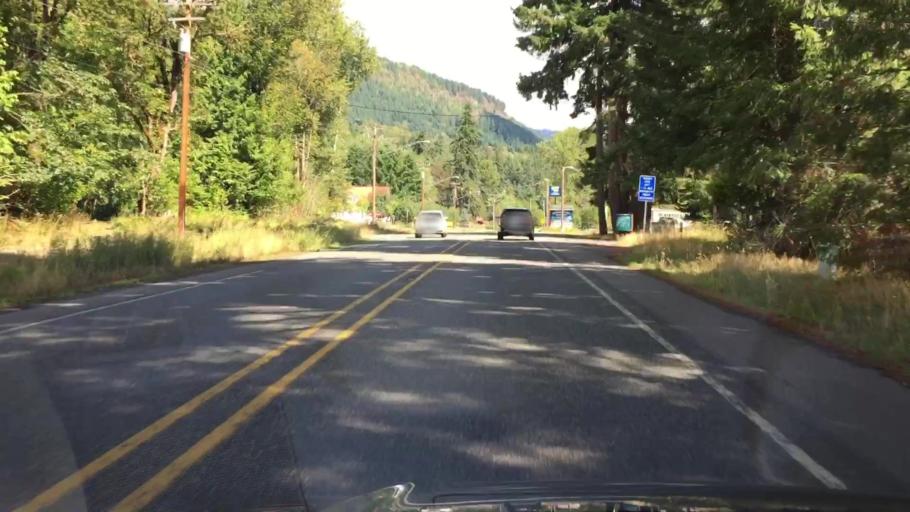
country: US
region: Washington
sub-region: Pierce County
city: Eatonville
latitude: 46.7596
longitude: -122.0418
